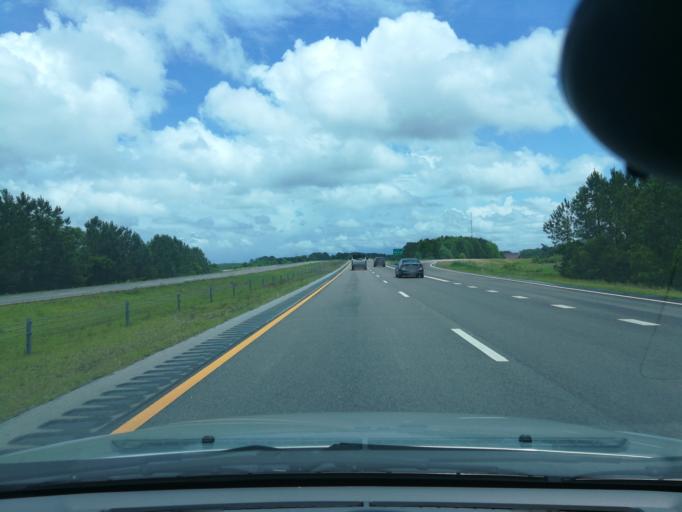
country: US
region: North Carolina
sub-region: Tyrrell County
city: Columbia
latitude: 35.9031
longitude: -76.3242
